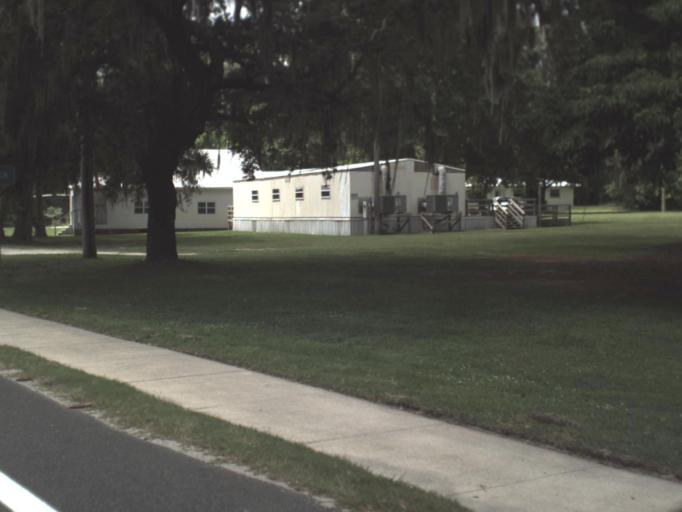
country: US
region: Florida
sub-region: Union County
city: Lake Butler
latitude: 29.9327
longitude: -82.4233
